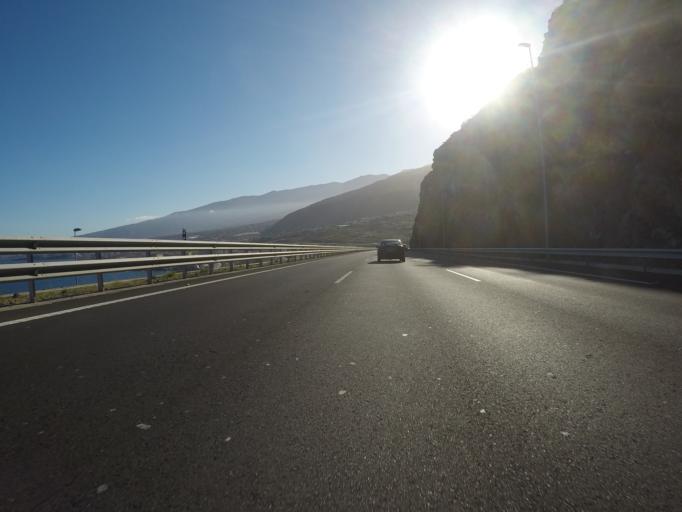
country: ES
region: Canary Islands
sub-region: Provincia de Santa Cruz de Tenerife
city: Candelaria
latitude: 28.3853
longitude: -16.3538
